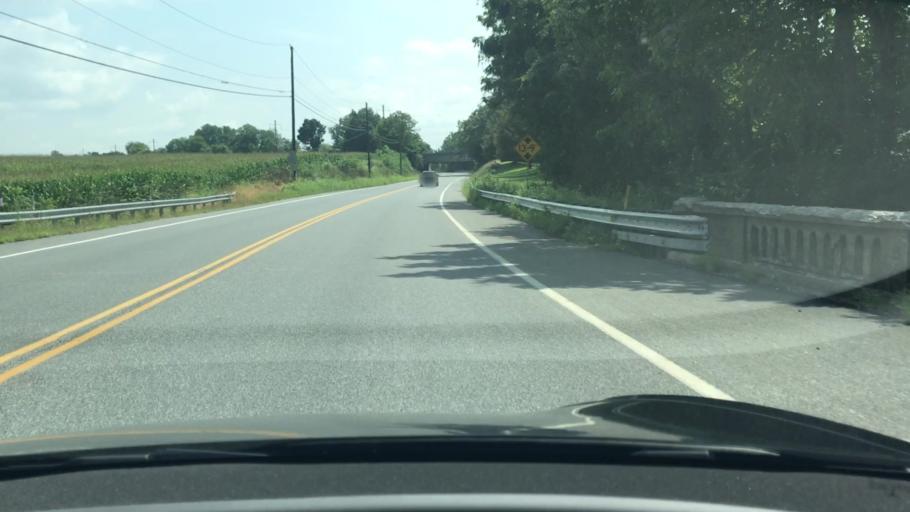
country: US
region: Pennsylvania
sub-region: Lancaster County
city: Salunga
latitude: 40.1091
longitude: -76.4504
